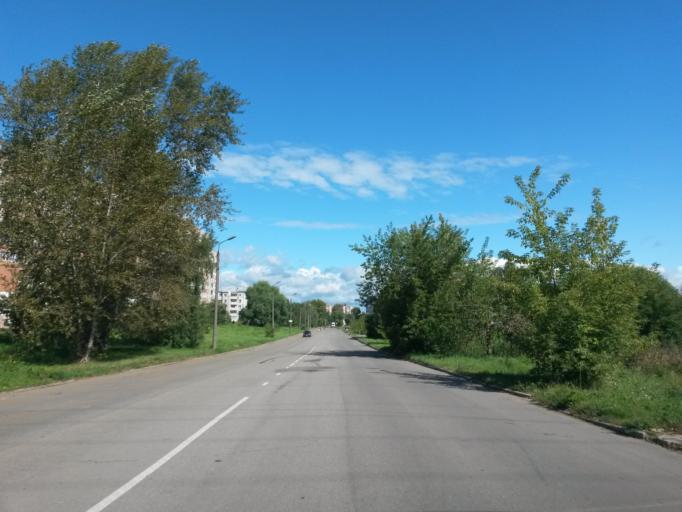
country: RU
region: Jaroslavl
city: Yaroslavl
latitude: 57.5832
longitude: 39.8658
